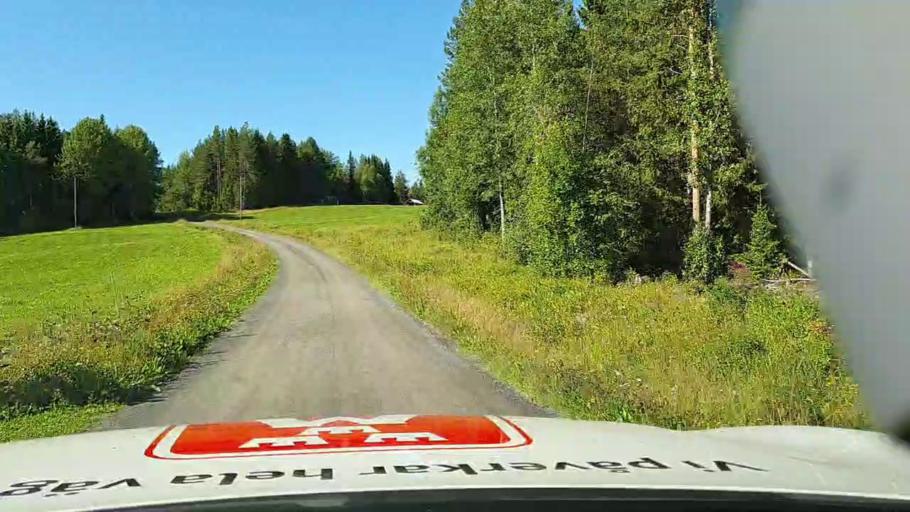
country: SE
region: Jaemtland
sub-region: OEstersunds Kommun
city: Lit
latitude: 63.7736
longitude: 14.6533
